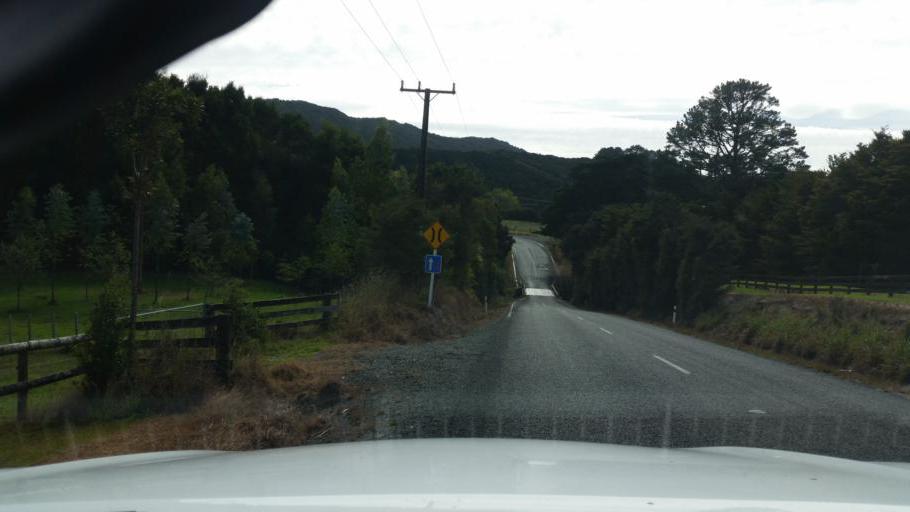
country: NZ
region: Auckland
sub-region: Auckland
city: Wellsford
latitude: -36.0879
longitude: 174.5348
